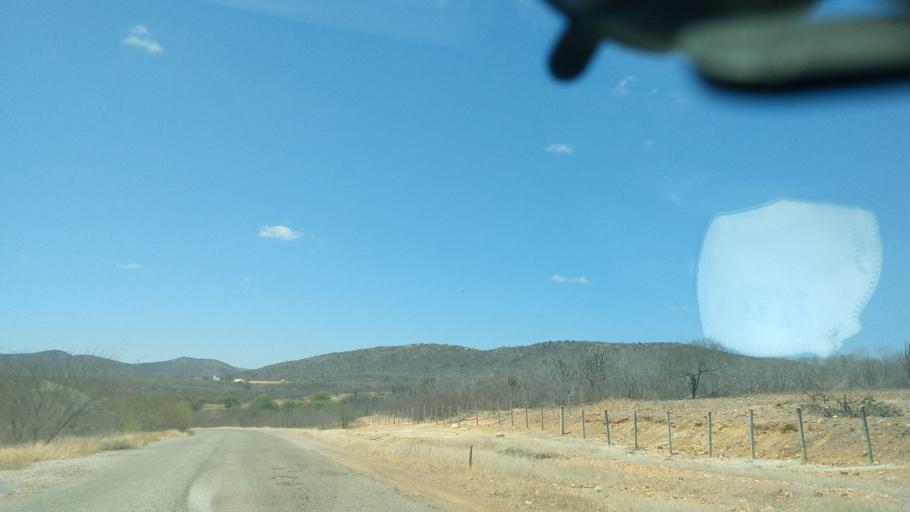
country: BR
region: Rio Grande do Norte
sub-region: Sao Tome
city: Sao Tome
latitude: -5.9692
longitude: -36.1311
